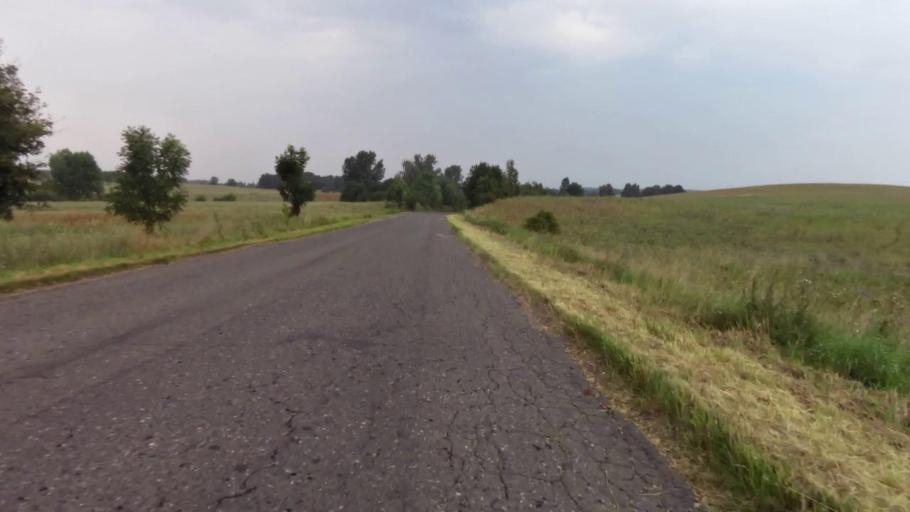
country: PL
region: West Pomeranian Voivodeship
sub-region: Powiat lobeski
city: Wegorzyno
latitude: 53.5035
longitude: 15.6458
